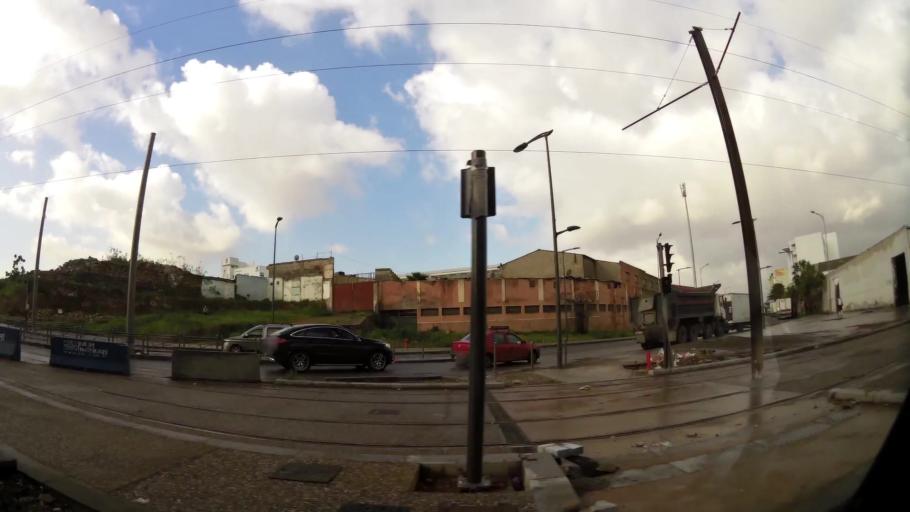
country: MA
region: Grand Casablanca
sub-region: Mediouna
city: Tit Mellil
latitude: 33.5947
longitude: -7.5414
